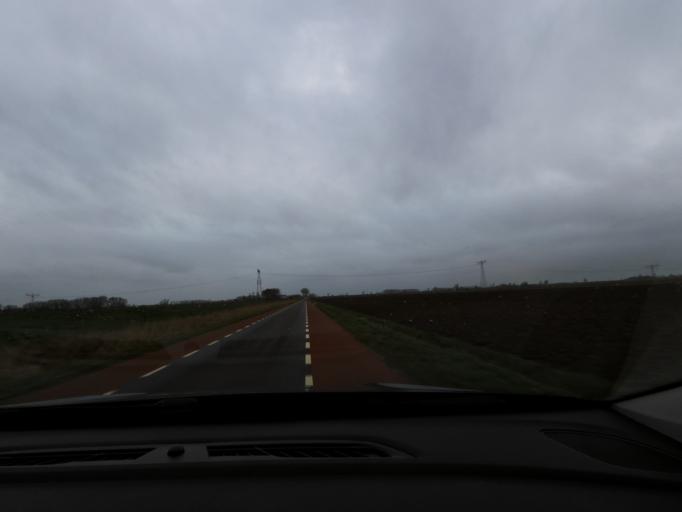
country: NL
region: North Brabant
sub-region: Gemeente Waalwijk
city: Waspik
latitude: 51.7009
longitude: 4.9843
